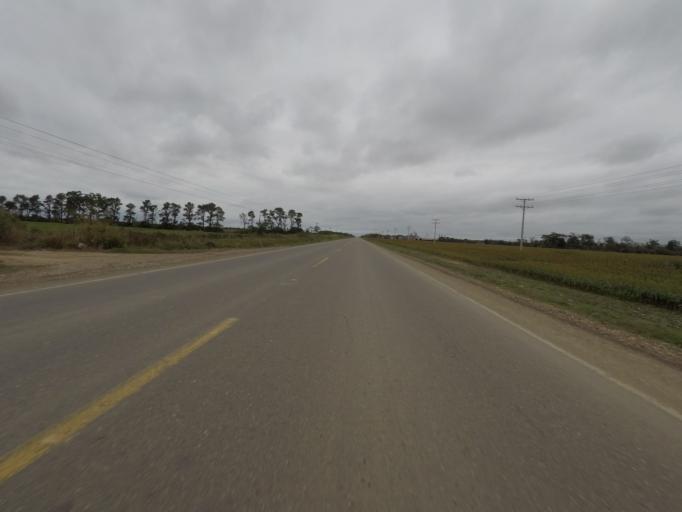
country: BO
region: Santa Cruz
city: Okinawa Numero Uno
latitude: -17.2392
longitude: -62.5554
